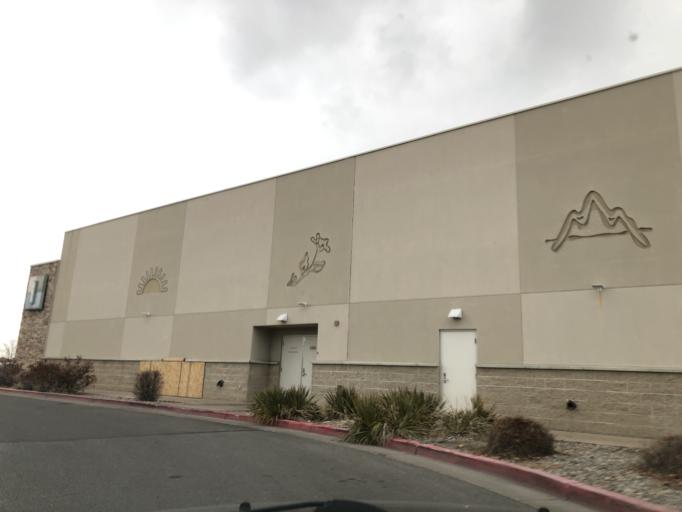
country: US
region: Utah
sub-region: Cache County
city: Logan
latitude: 41.7555
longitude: -111.8319
